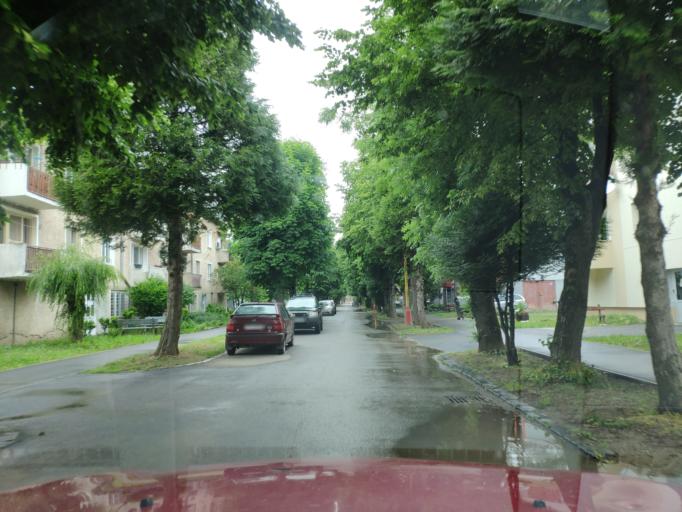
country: SK
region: Kosicky
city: Cierna nad Tisou
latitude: 48.4157
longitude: 22.0896
